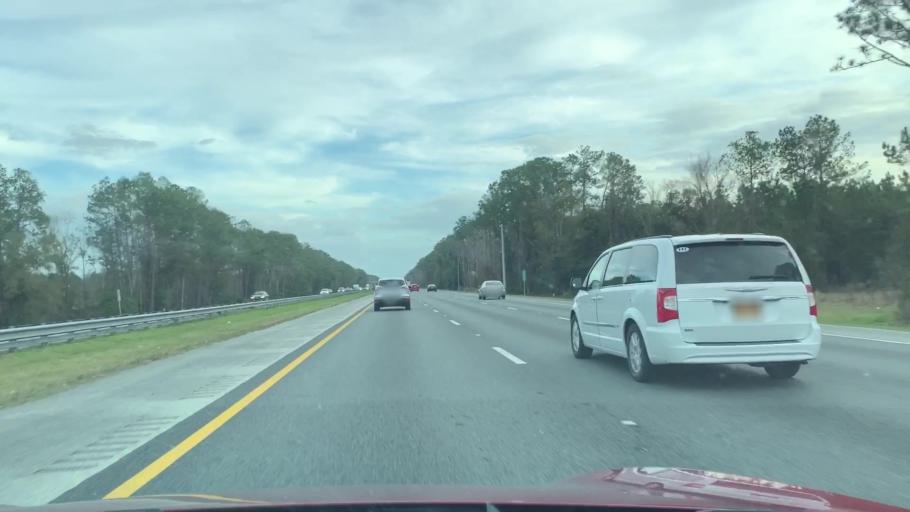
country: US
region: Florida
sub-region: Saint Johns County
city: Fruit Cove
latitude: 30.0195
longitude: -81.4825
